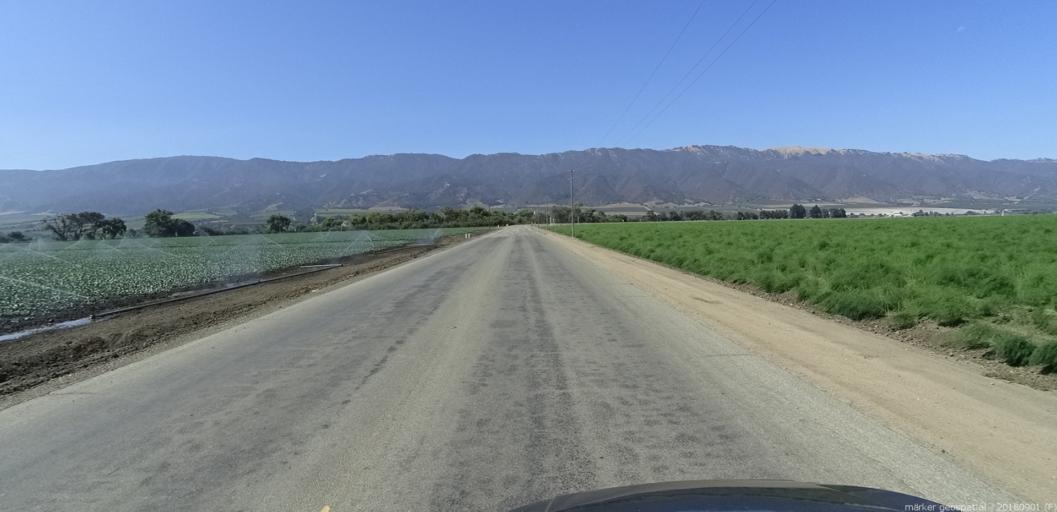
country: US
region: California
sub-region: Monterey County
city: Gonzales
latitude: 36.4913
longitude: -121.4604
